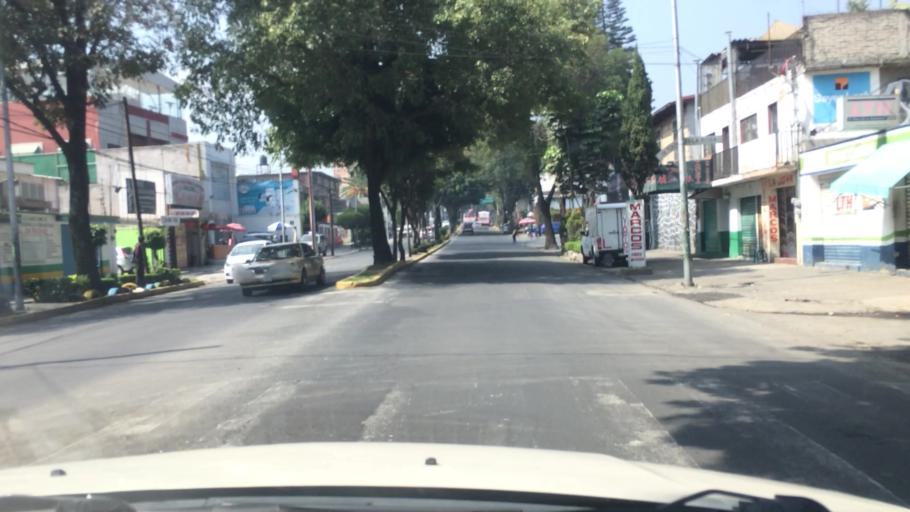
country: MX
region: Mexico City
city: Tlalpan
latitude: 19.2843
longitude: -99.1643
